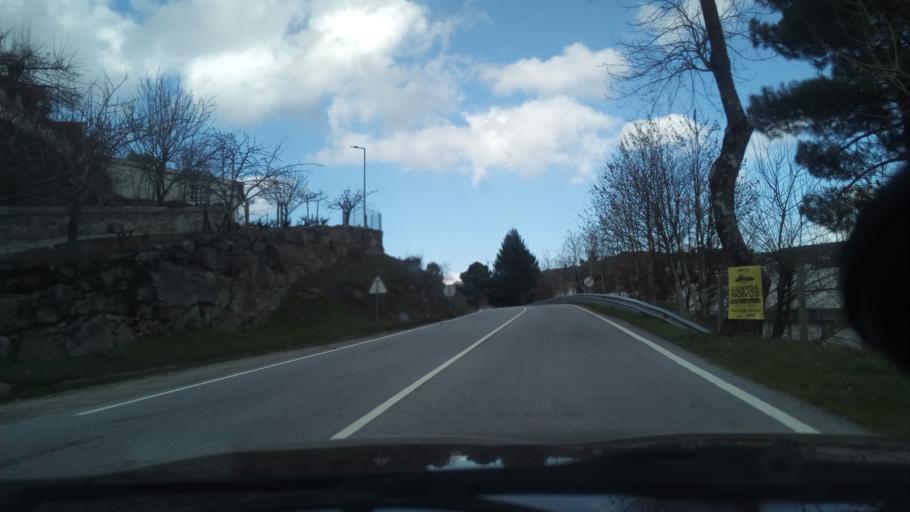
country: PT
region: Guarda
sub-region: Guarda
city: Guarda
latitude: 40.5387
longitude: -7.3044
